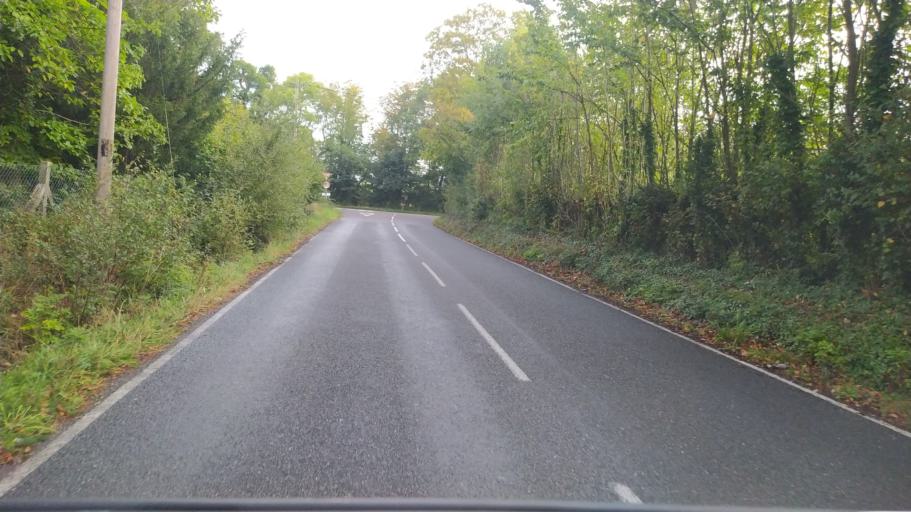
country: GB
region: England
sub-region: Hampshire
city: Romsey
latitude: 50.9876
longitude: -1.5331
